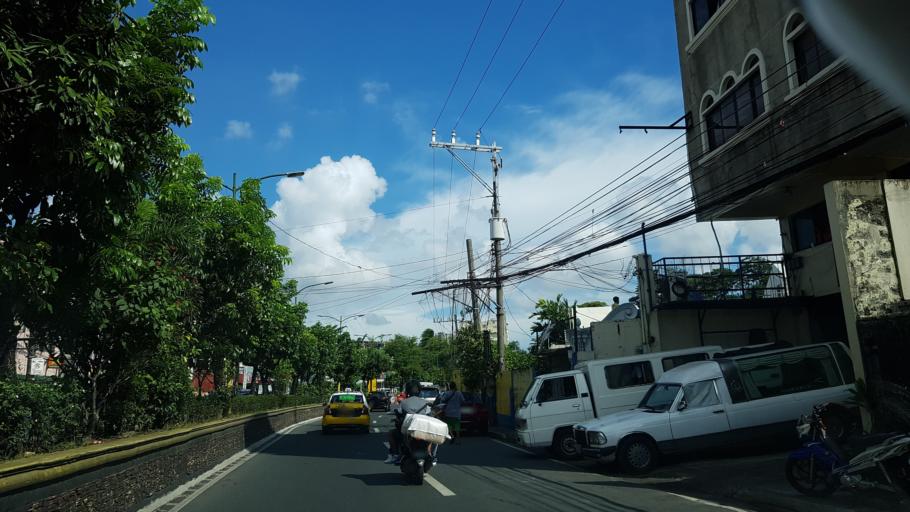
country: PH
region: Metro Manila
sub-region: Mandaluyong
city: Mandaluyong City
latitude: 14.5854
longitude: 121.0265
